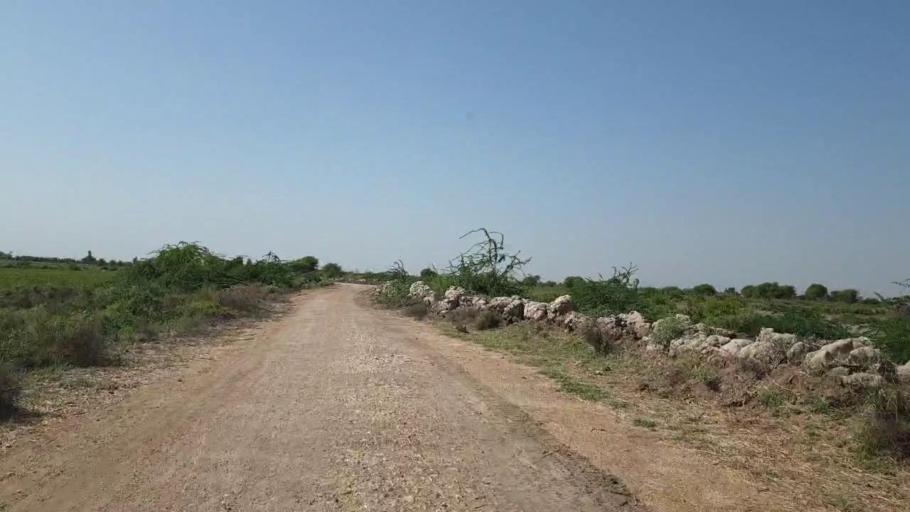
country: PK
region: Sindh
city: Tando Bago
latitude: 24.7062
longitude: 69.0552
